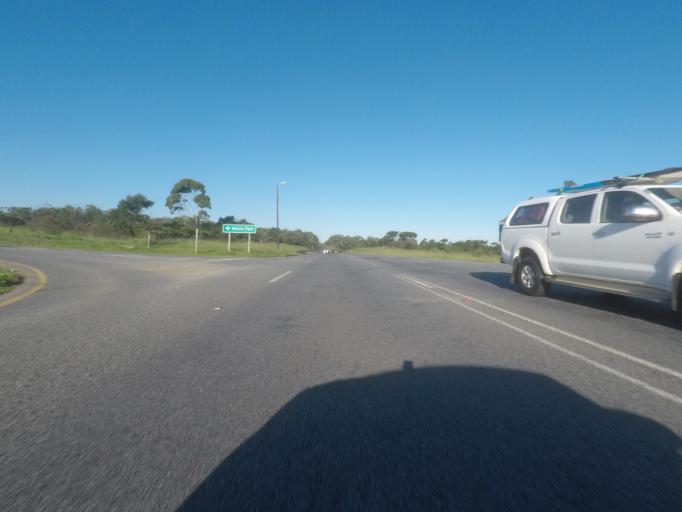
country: ZA
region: Eastern Cape
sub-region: Buffalo City Metropolitan Municipality
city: East London
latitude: -33.0488
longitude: 27.8179
